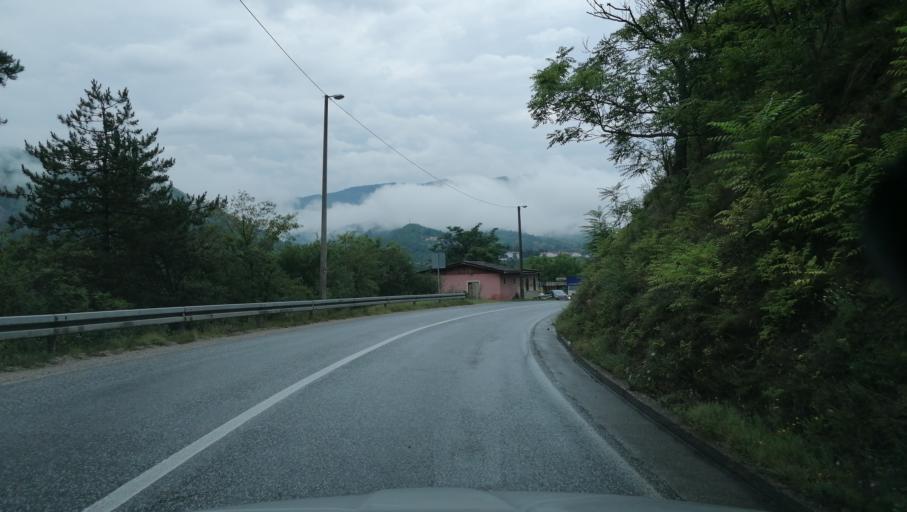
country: BA
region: Republika Srpska
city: Visegrad
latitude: 43.7830
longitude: 19.3008
